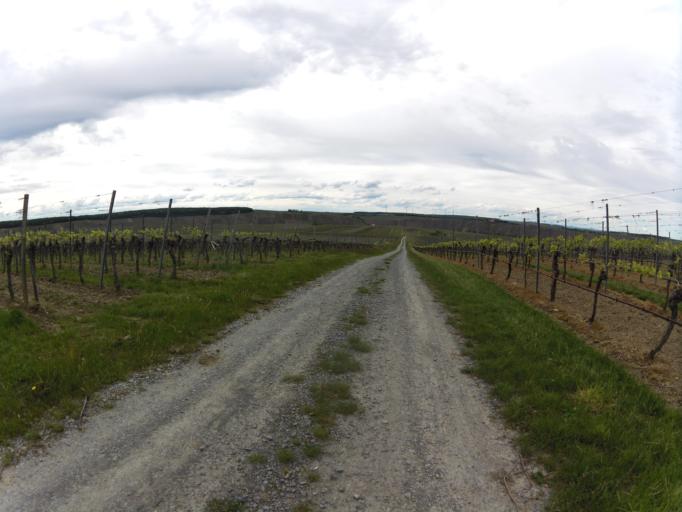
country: DE
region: Bavaria
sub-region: Regierungsbezirk Unterfranken
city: Sommerach
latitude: 49.8474
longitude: 10.1956
